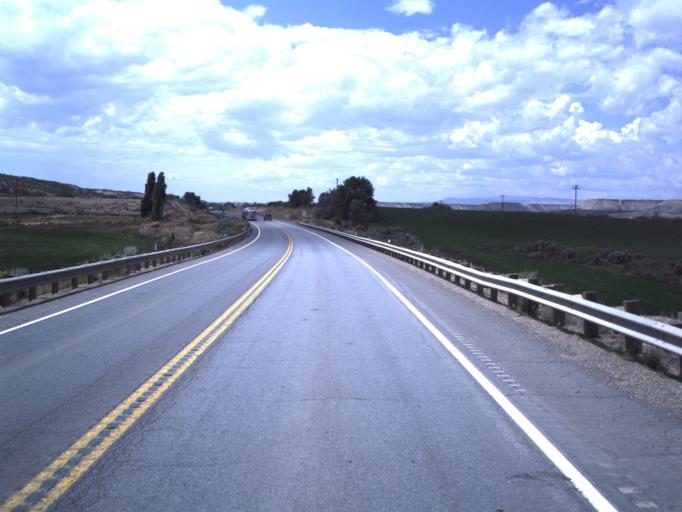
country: US
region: Utah
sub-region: Duchesne County
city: Duchesne
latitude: 40.1691
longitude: -110.3008
